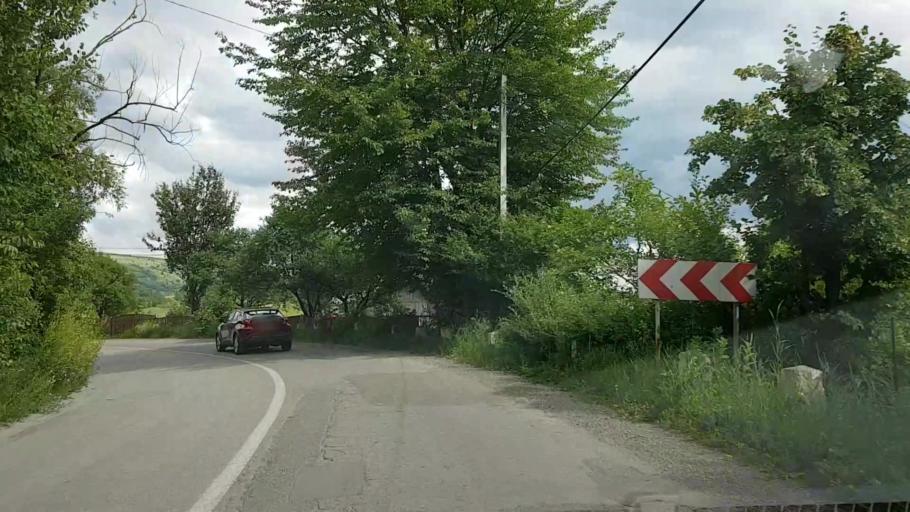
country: RO
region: Neamt
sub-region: Comuna Hangu
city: Hangu
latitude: 47.0457
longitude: 26.0422
